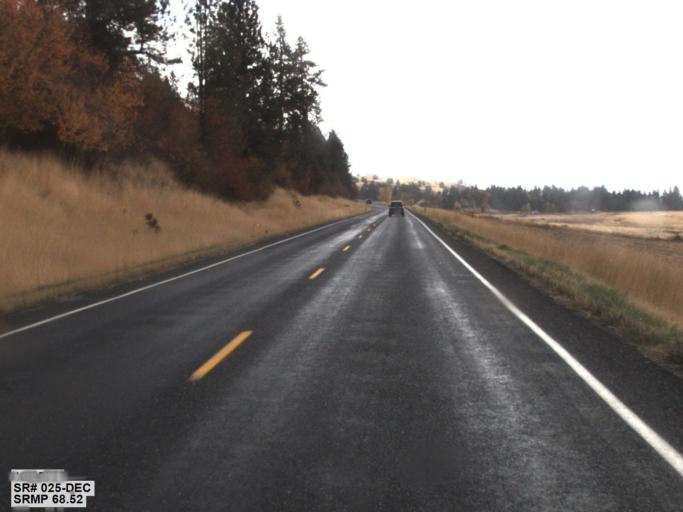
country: US
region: Washington
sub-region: Stevens County
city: Kettle Falls
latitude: 48.4587
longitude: -118.1794
